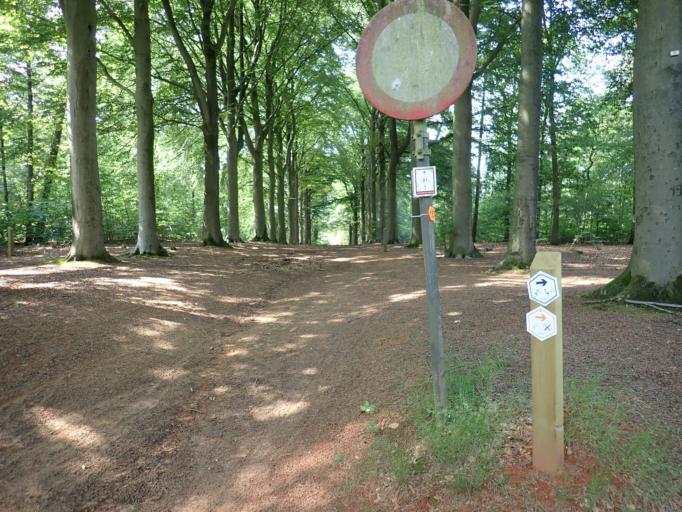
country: BE
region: Flanders
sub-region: Provincie Antwerpen
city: Kasterlee
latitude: 51.2280
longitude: 4.9561
